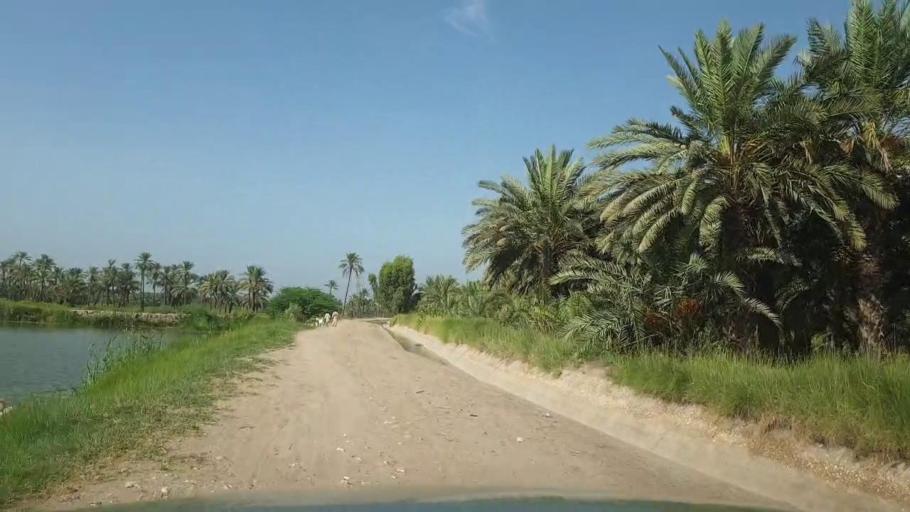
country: PK
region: Sindh
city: Rohri
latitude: 27.6576
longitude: 68.8832
